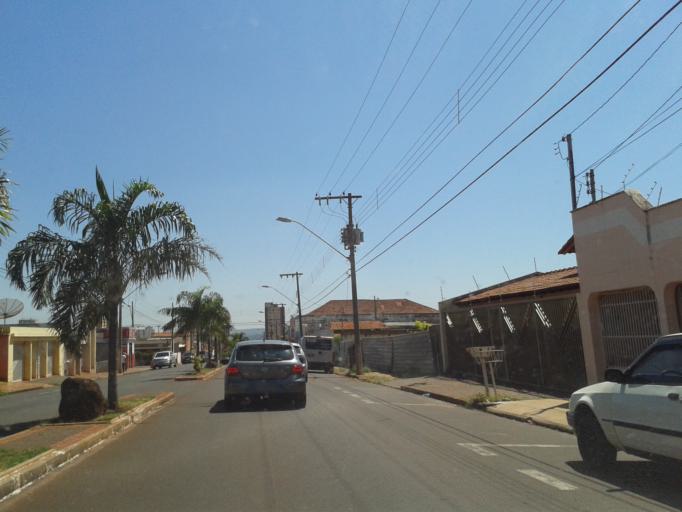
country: BR
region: Minas Gerais
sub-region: Ituiutaba
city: Ituiutaba
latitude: -18.9808
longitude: -49.4584
